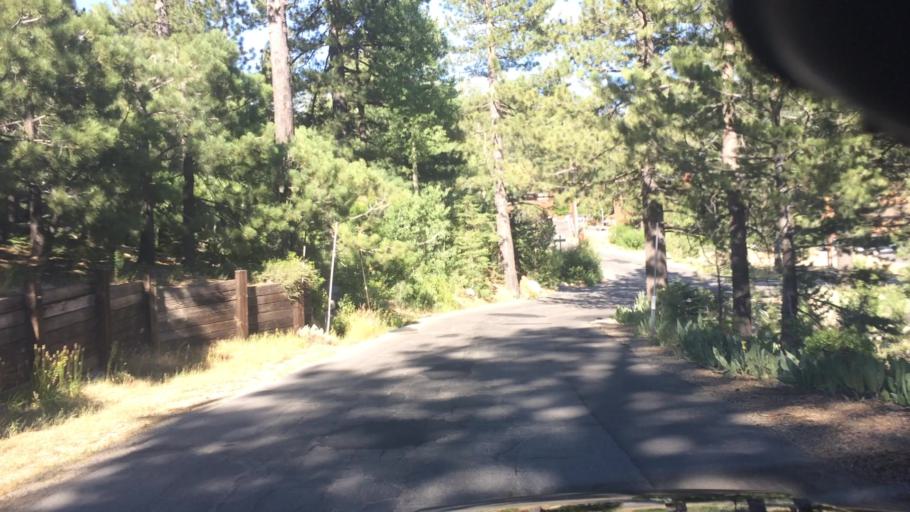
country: US
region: California
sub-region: Placer County
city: Sunnyside-Tahoe City
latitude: 39.2001
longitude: -120.2298
